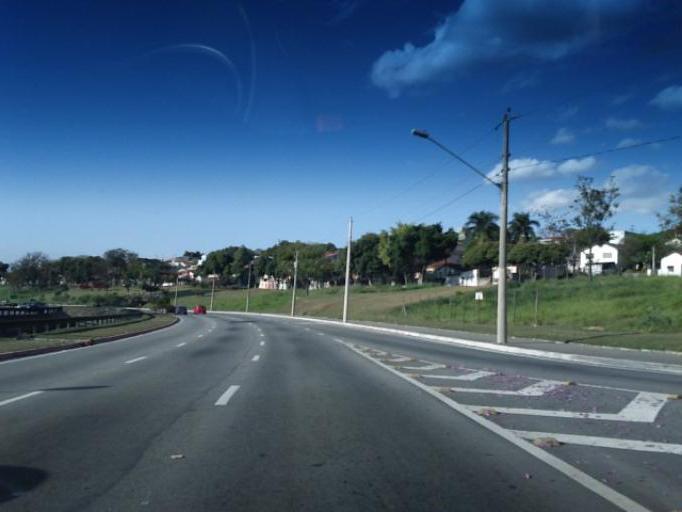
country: BR
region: Sao Paulo
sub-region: Sao Jose Dos Campos
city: Sao Jose dos Campos
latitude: -23.1870
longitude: -45.8785
